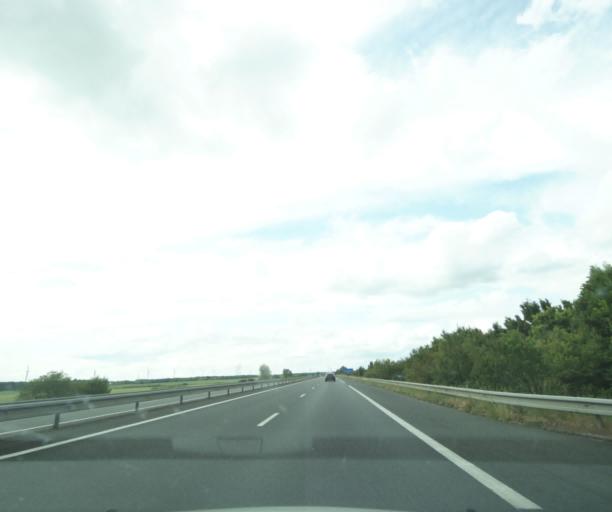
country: FR
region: Centre
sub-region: Departement du Cher
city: Marmagne
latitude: 47.0809
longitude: 2.2682
